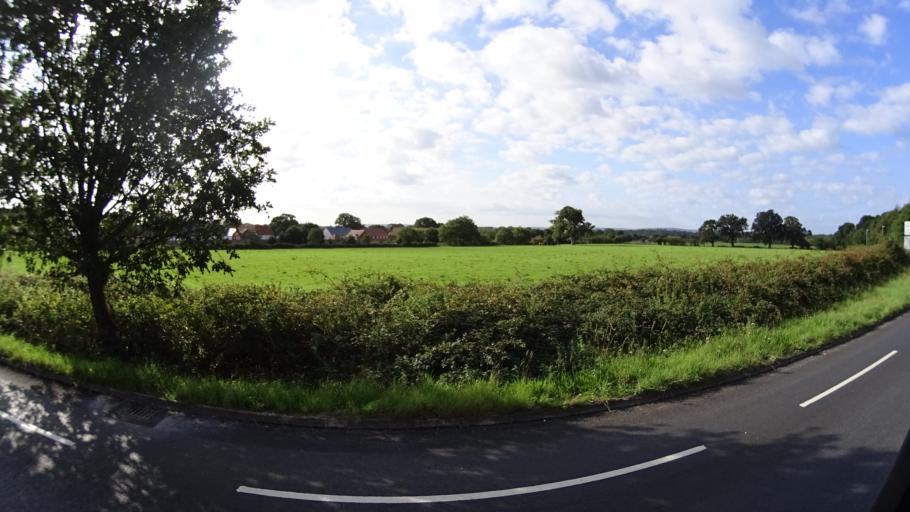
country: GB
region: England
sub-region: Dorset
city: Lytchett Matravers
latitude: 50.7408
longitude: -2.0482
